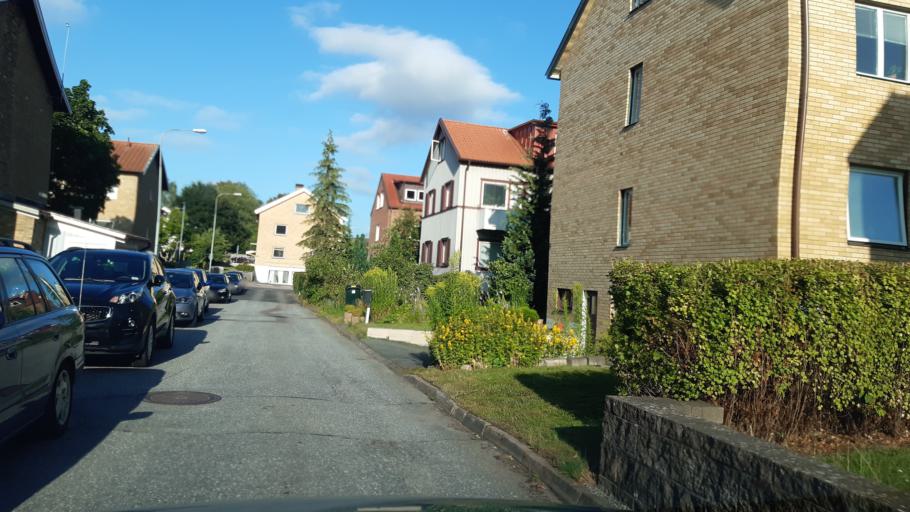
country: SE
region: Vaestra Goetaland
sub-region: Partille Kommun
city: Partille
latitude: 57.7200
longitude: 12.0643
